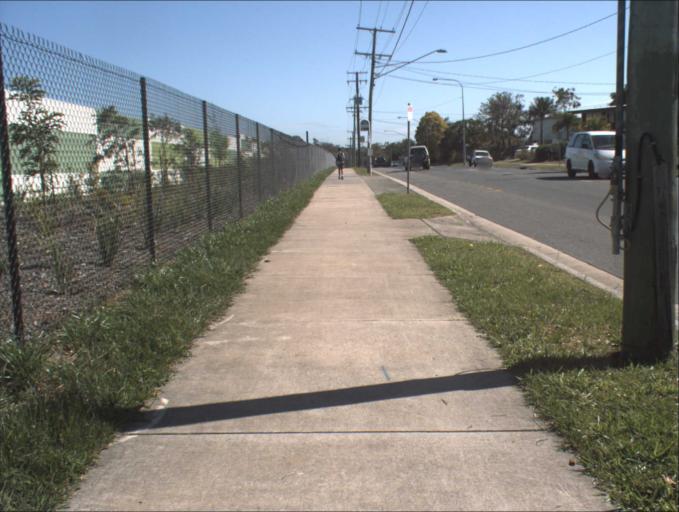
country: AU
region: Queensland
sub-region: Logan
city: Logan City
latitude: -27.6485
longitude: 153.0991
